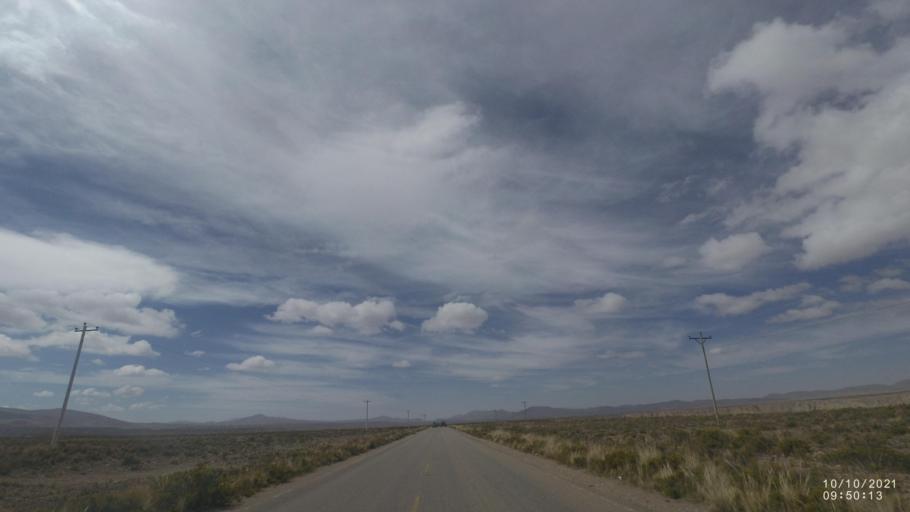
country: BO
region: La Paz
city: Colquiri
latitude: -17.2394
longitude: -67.3341
